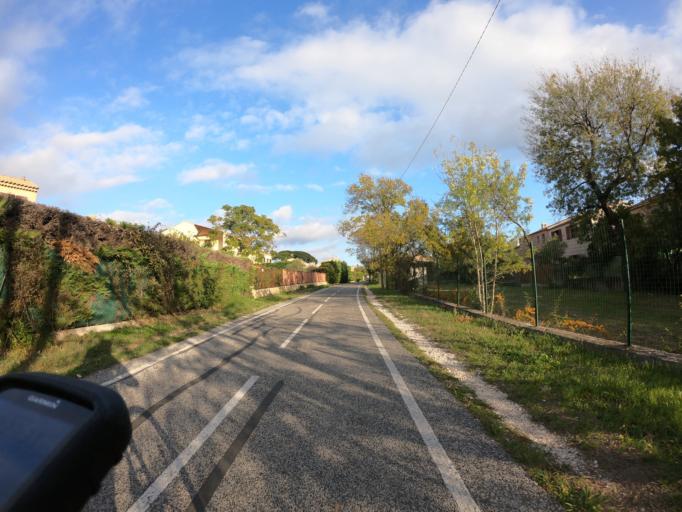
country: FR
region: Provence-Alpes-Cote d'Azur
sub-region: Departement du Var
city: La Garde
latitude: 43.1116
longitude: 5.9938
